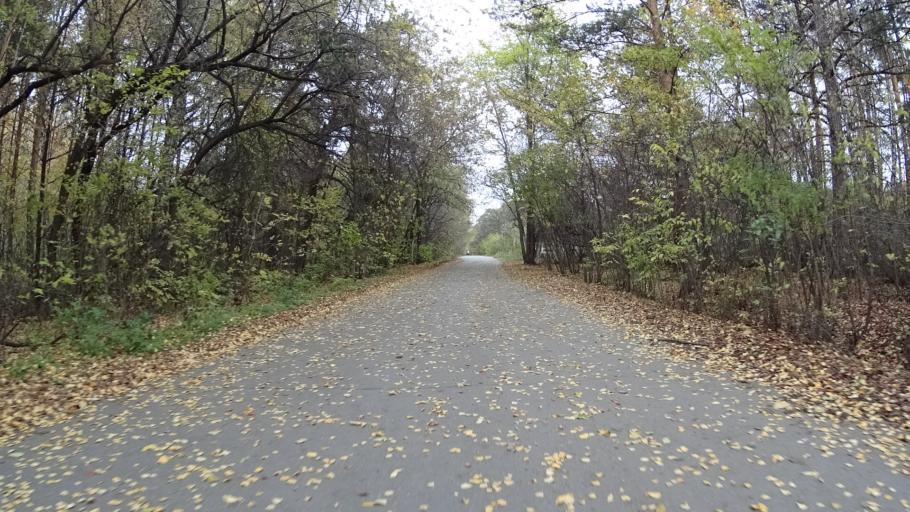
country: RU
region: Chelyabinsk
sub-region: Gorod Chelyabinsk
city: Chelyabinsk
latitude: 55.1475
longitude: 61.3543
